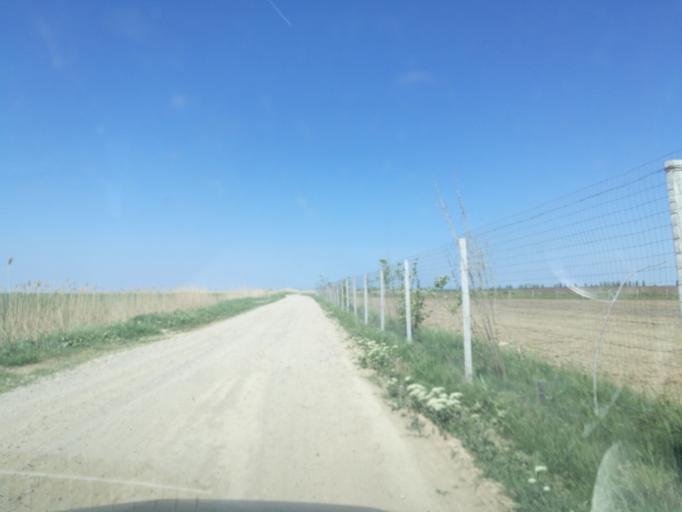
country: RO
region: Ialomita
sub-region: Comuna Adancata
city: Adancata
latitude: 44.7819
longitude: 26.4670
